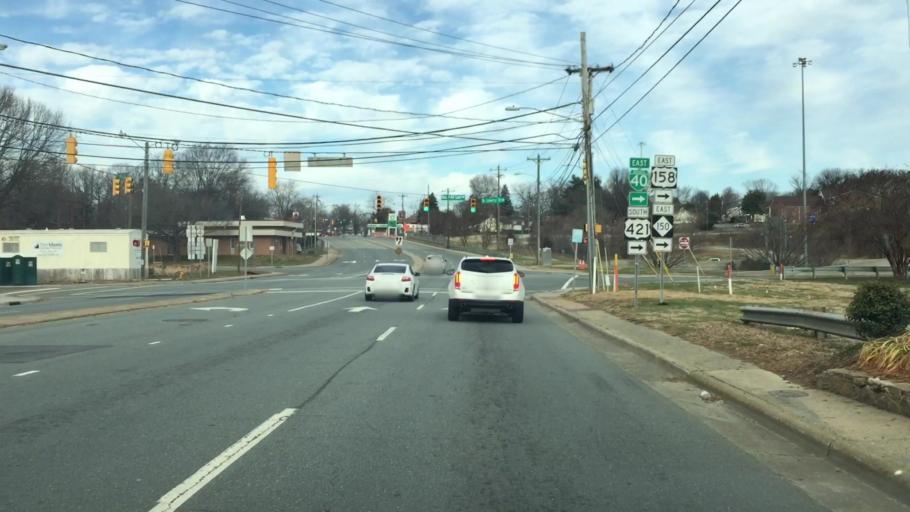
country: US
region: North Carolina
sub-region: Forsyth County
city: Winston-Salem
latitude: 36.0935
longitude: -80.2276
